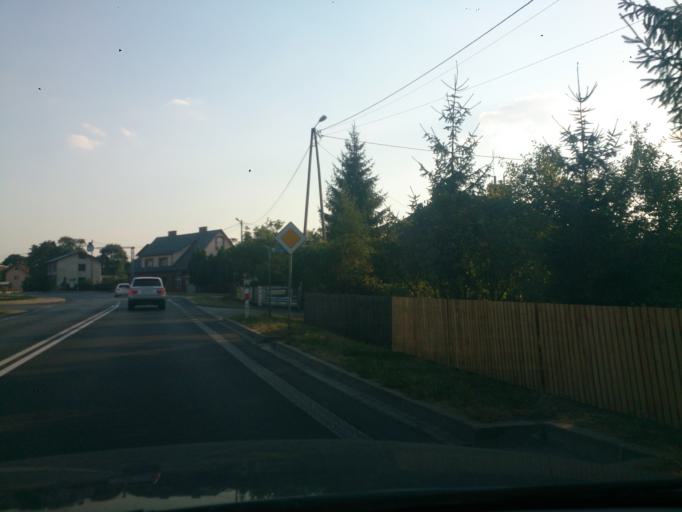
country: PL
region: Subcarpathian Voivodeship
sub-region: Powiat tarnobrzeski
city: Nowa Deba
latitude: 50.4302
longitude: 21.7511
